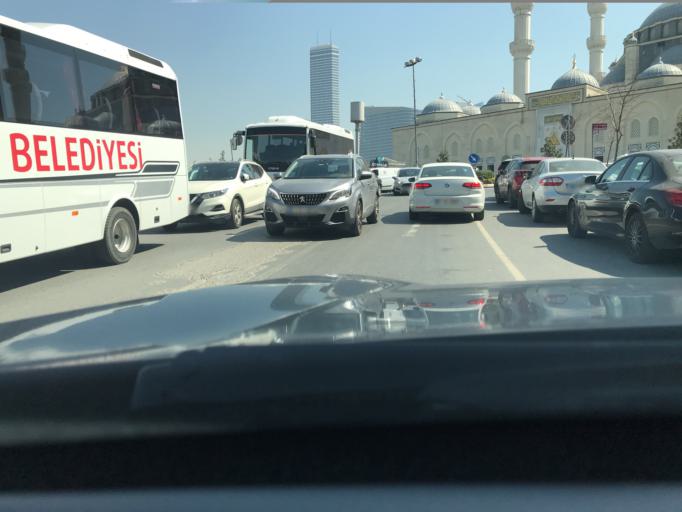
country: TR
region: Istanbul
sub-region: Atasehir
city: Atasehir
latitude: 40.9966
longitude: 29.1112
